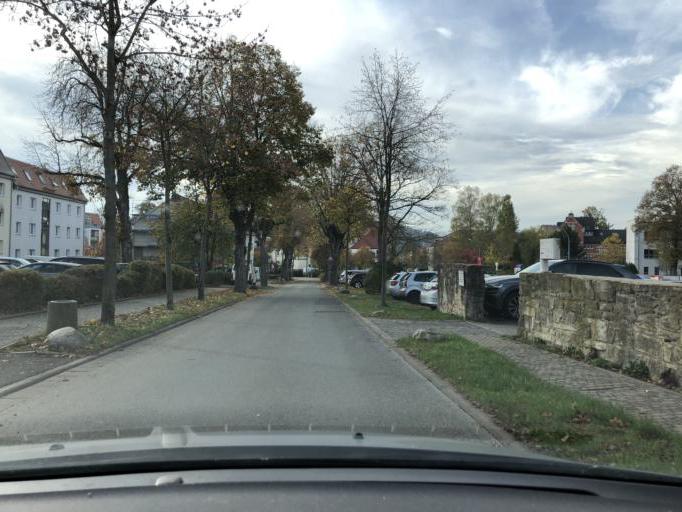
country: DE
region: Thuringia
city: Hildburghausen
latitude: 50.4274
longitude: 10.7292
